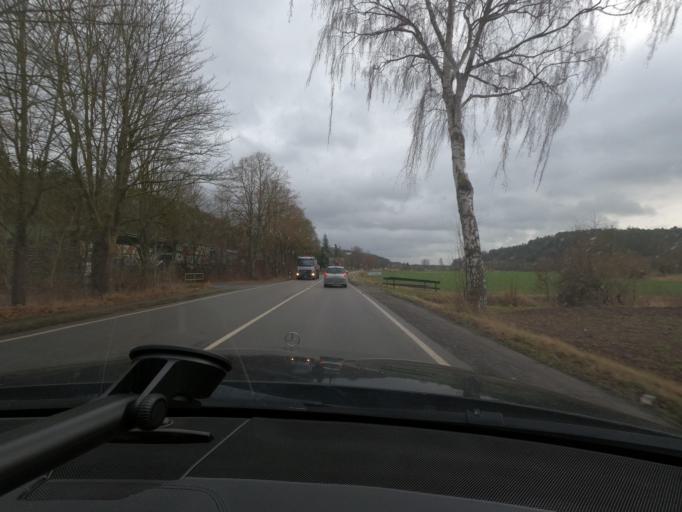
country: DE
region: Hesse
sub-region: Regierungsbezirk Kassel
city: Volkmarsen
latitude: 51.4074
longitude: 9.1361
